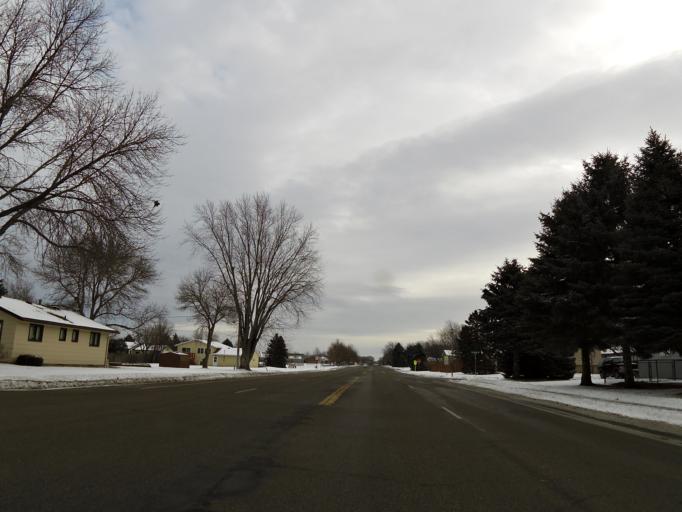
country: US
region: Minnesota
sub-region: Scott County
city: Shakopee
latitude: 44.7883
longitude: -93.5160
